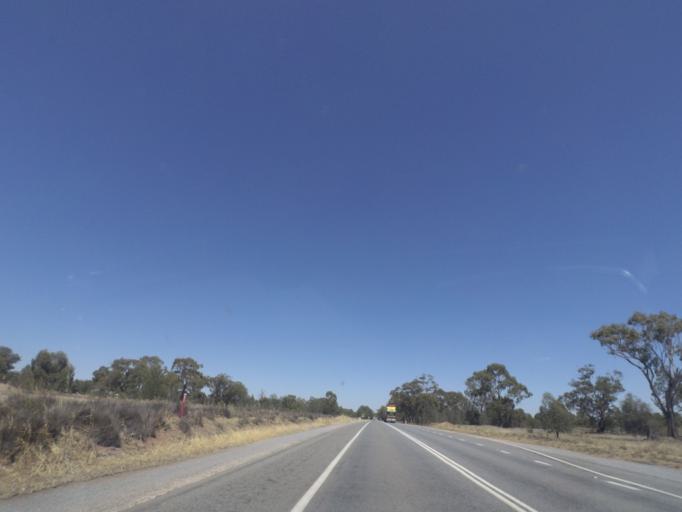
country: AU
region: New South Wales
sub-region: Narrandera
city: Narrandera
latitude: -34.7361
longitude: 146.6003
